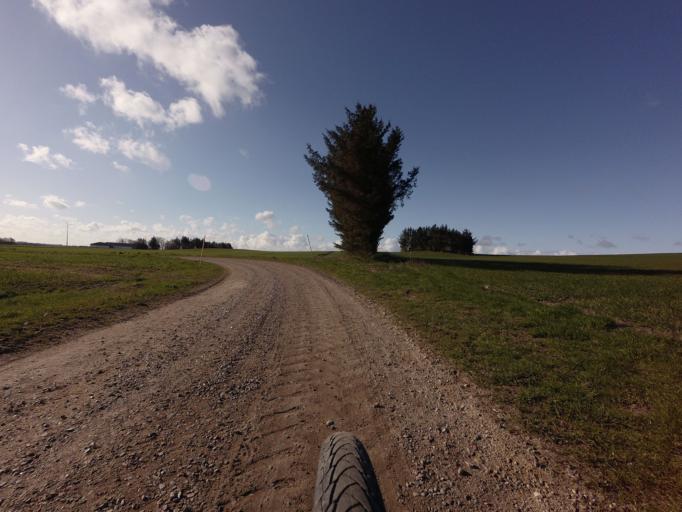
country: DK
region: North Denmark
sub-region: Hjorring Kommune
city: Vra
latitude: 57.3672
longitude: 9.8137
